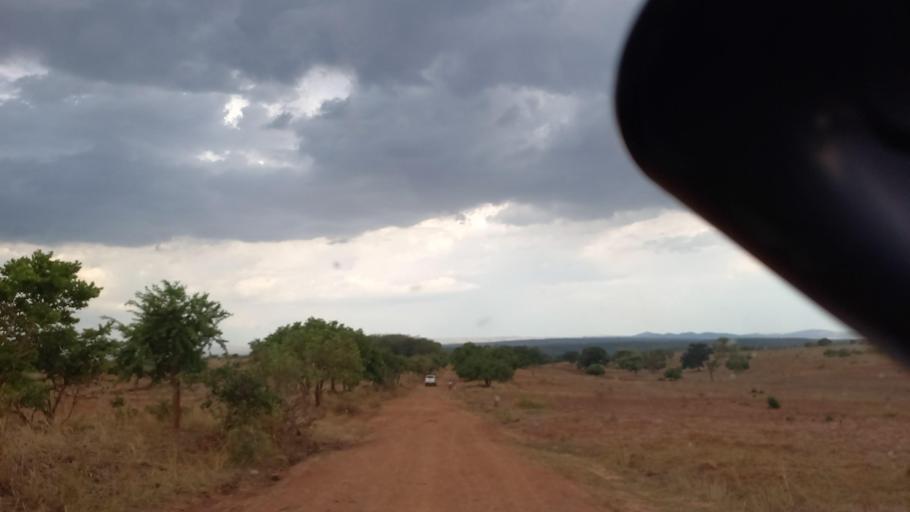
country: ZM
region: Lusaka
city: Kafue
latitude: -16.1344
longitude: 28.0561
